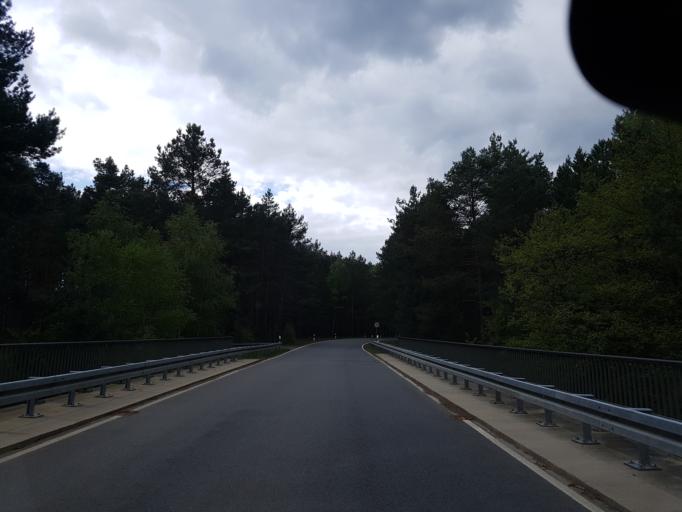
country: DE
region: Brandenburg
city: Altdobern
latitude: 51.6441
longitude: 13.9773
